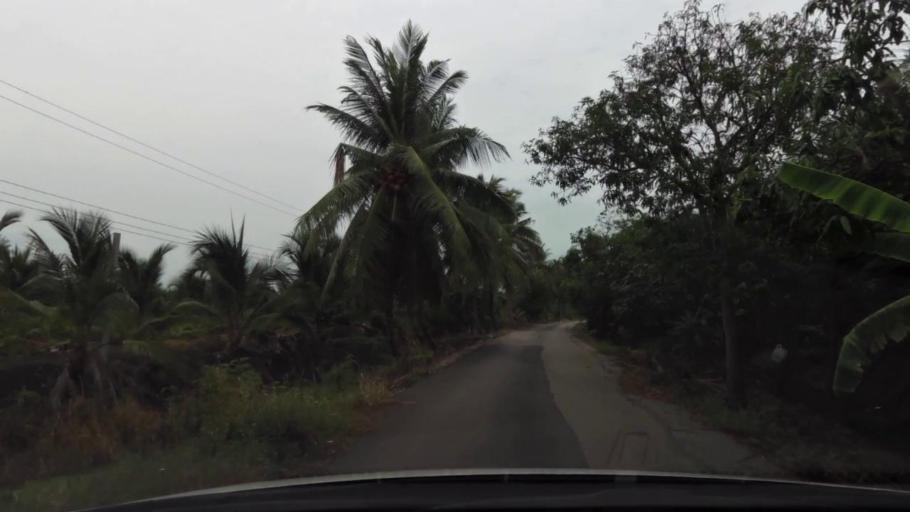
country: TH
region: Samut Sakhon
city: Ban Phaeo
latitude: 13.6043
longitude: 100.0288
